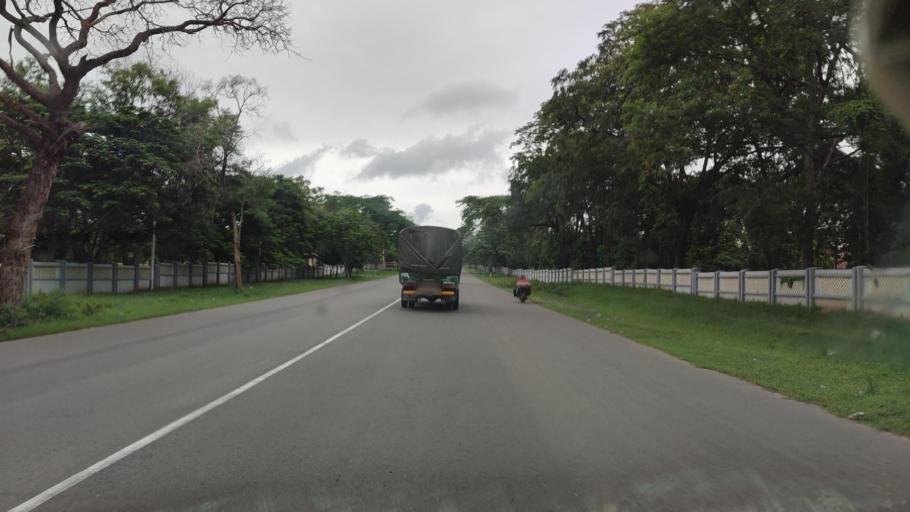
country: MM
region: Mandalay
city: Meiktila
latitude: 20.8491
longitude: 95.8873
